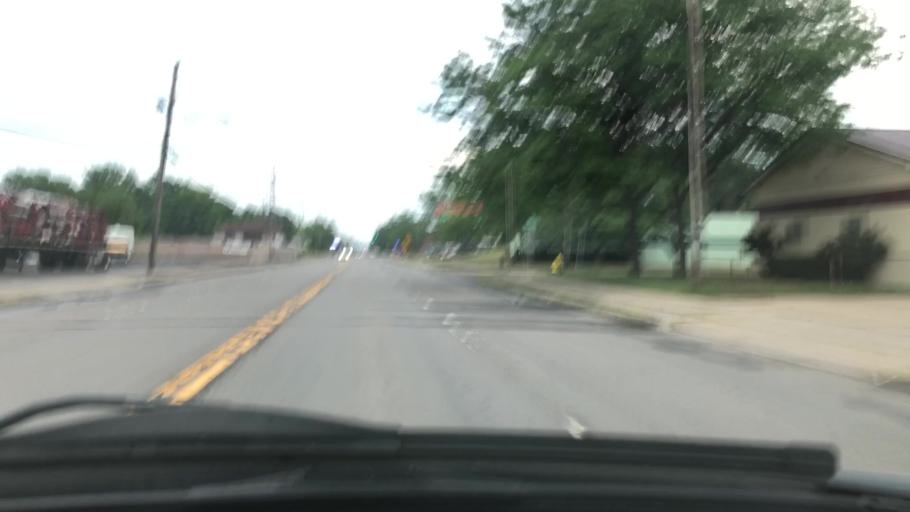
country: US
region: New York
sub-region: Erie County
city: Sloan
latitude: 42.8845
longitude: -78.7929
